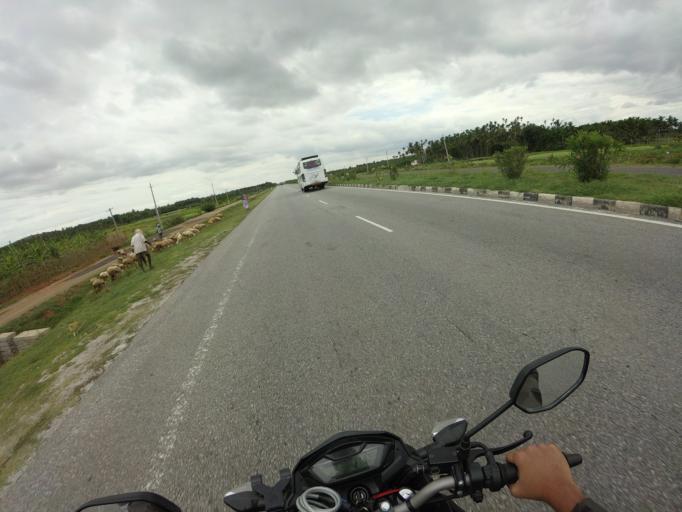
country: IN
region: Karnataka
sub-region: Tumkur
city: Kunigal
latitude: 13.0050
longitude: 77.0029
